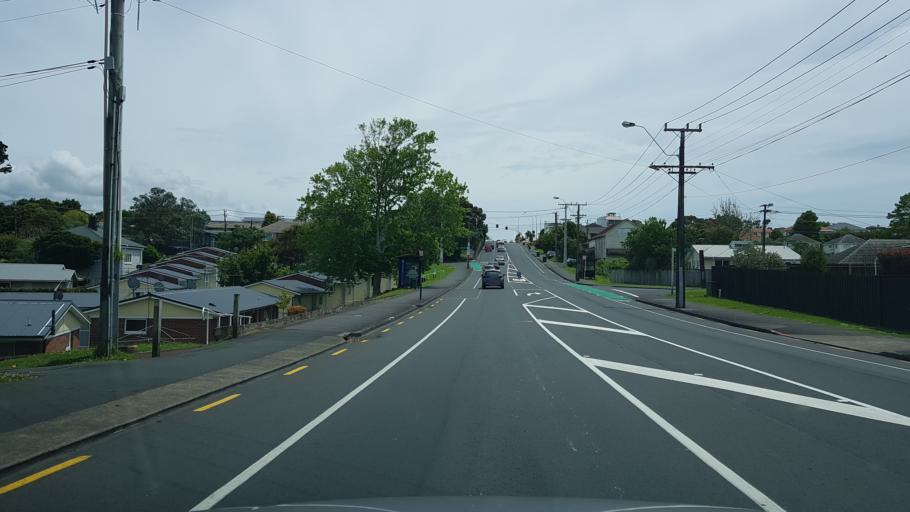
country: NZ
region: Auckland
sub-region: Auckland
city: North Shore
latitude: -36.8108
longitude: 174.7913
